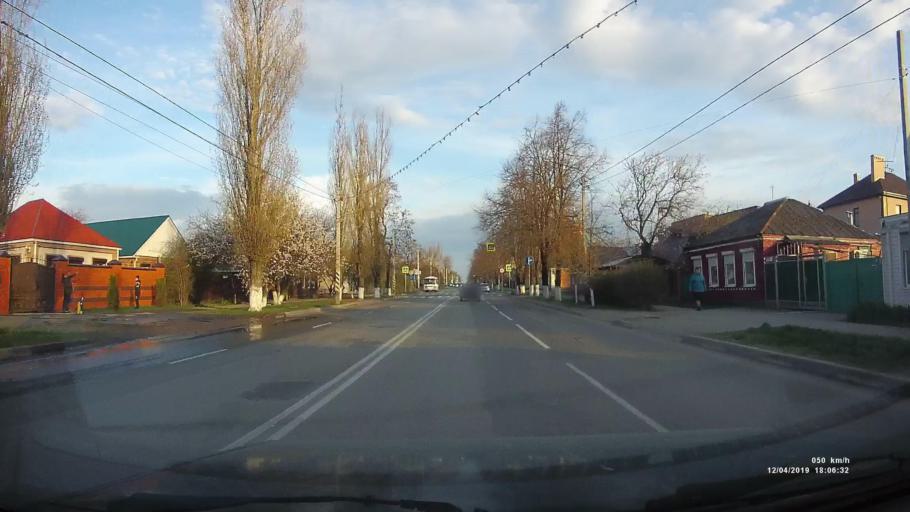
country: RU
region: Rostov
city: Azov
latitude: 47.0962
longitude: 39.4455
